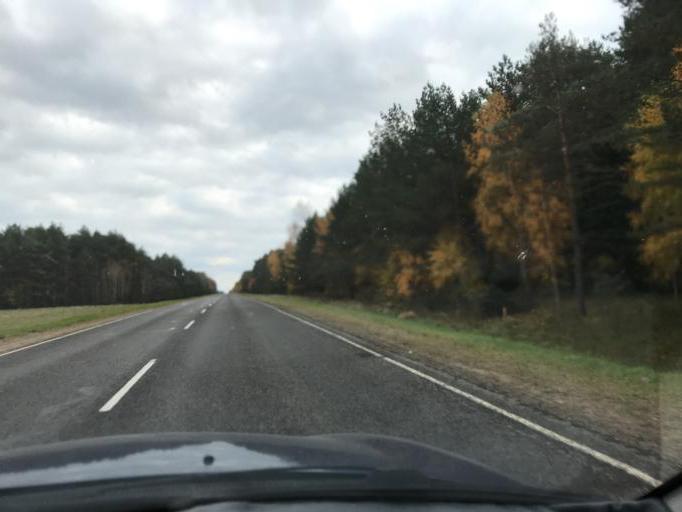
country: BY
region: Grodnenskaya
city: Lida
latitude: 53.7462
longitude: 25.2977
